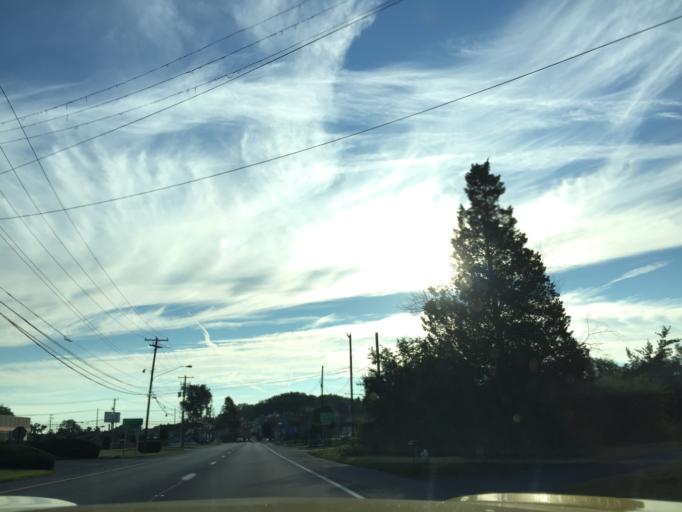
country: US
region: Pennsylvania
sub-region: Lehigh County
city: Dorneyville
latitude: 40.5788
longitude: -75.5241
